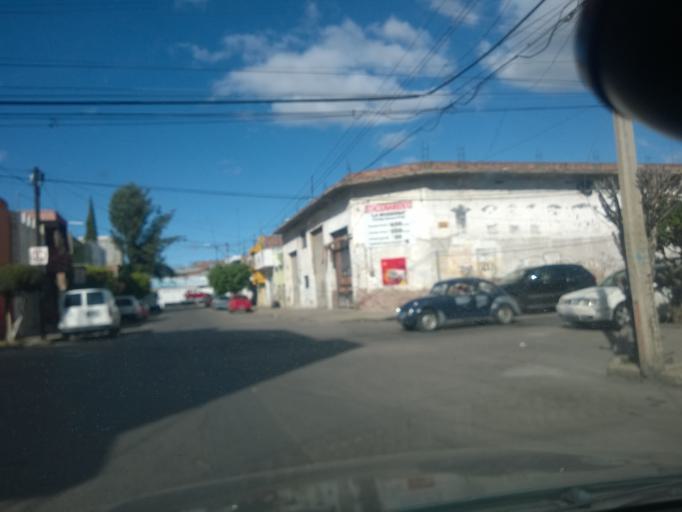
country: MX
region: Guanajuato
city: Leon
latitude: 21.1353
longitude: -101.6867
